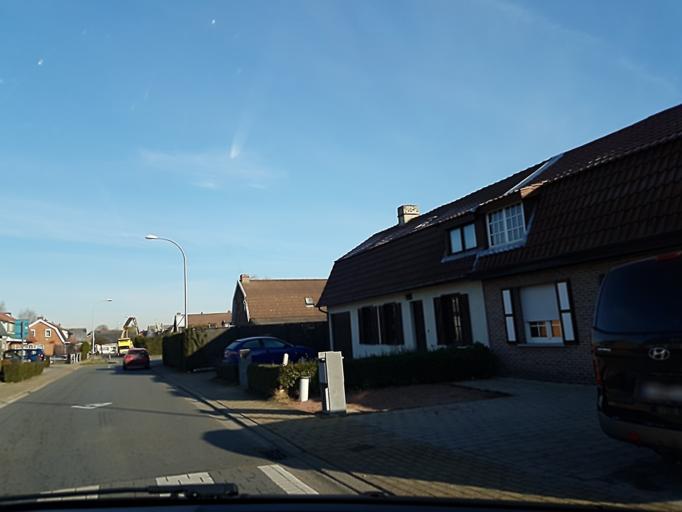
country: BE
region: Flanders
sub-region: Provincie Antwerpen
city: Willebroek
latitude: 51.0622
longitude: 4.3527
